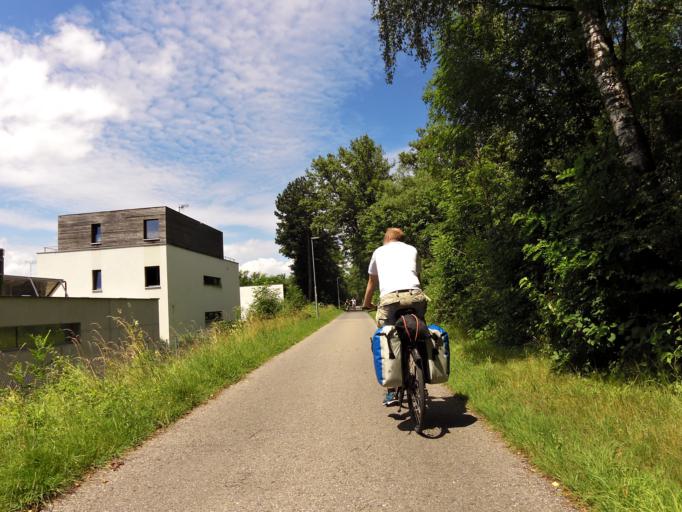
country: AT
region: Vorarlberg
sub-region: Politischer Bezirk Bregenz
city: Hard
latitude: 47.5003
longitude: 9.6944
